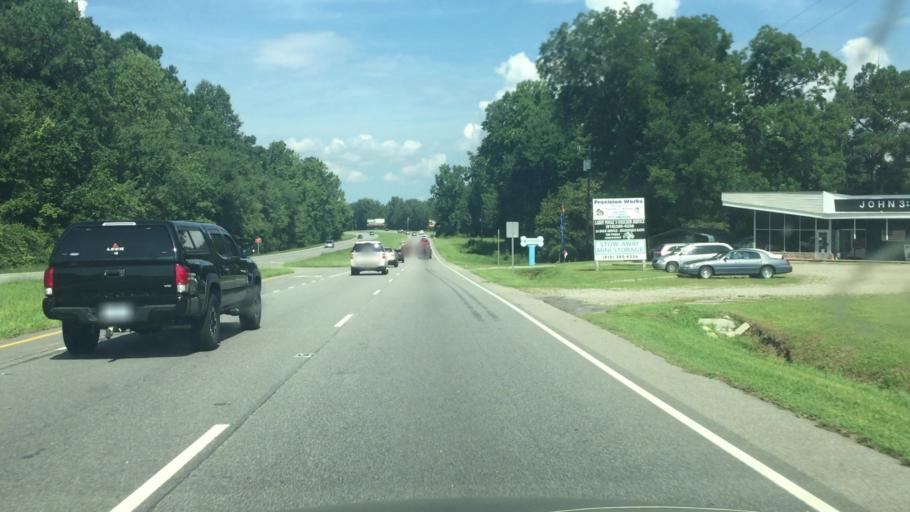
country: US
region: North Carolina
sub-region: Scotland County
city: Laurel Hill
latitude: 34.7958
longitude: -79.5158
